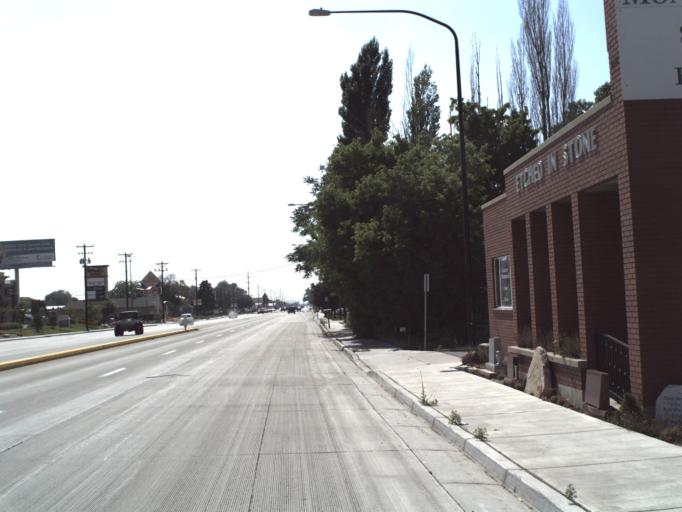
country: US
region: Utah
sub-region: Weber County
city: Ogden
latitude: 41.2444
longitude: -111.9761
